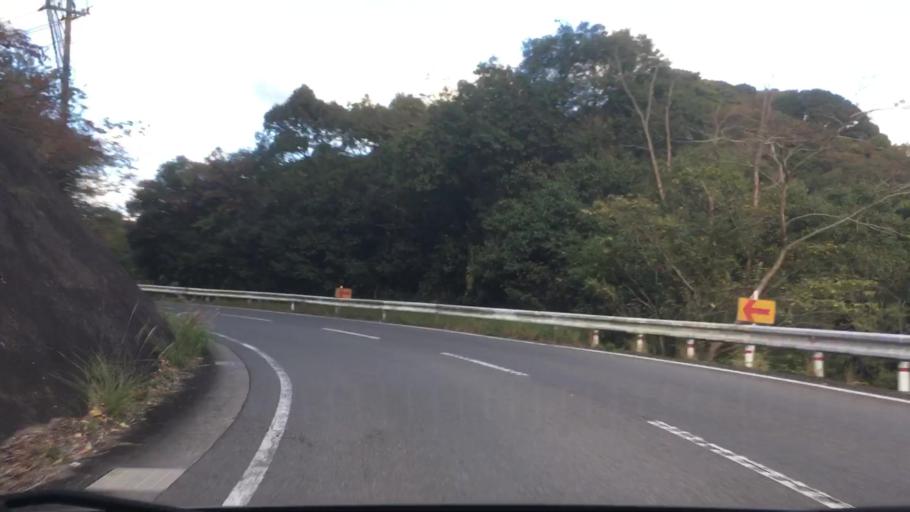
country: JP
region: Nagasaki
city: Sasebo
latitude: 32.9633
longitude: 129.6875
